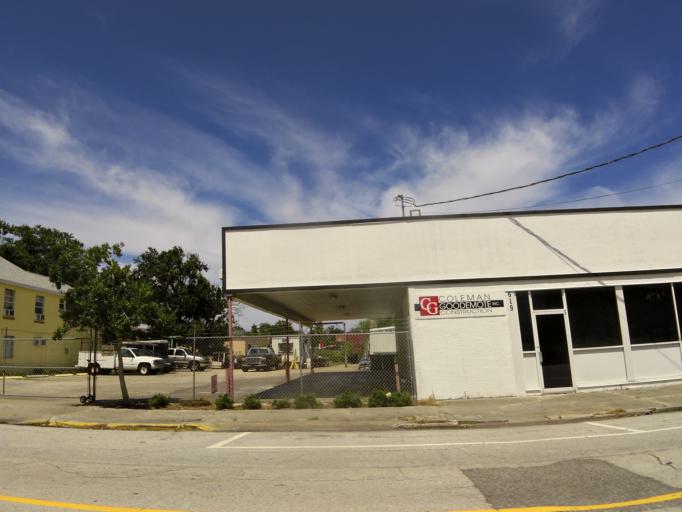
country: US
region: Florida
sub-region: Volusia County
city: Daytona Beach
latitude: 29.2242
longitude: -81.0246
